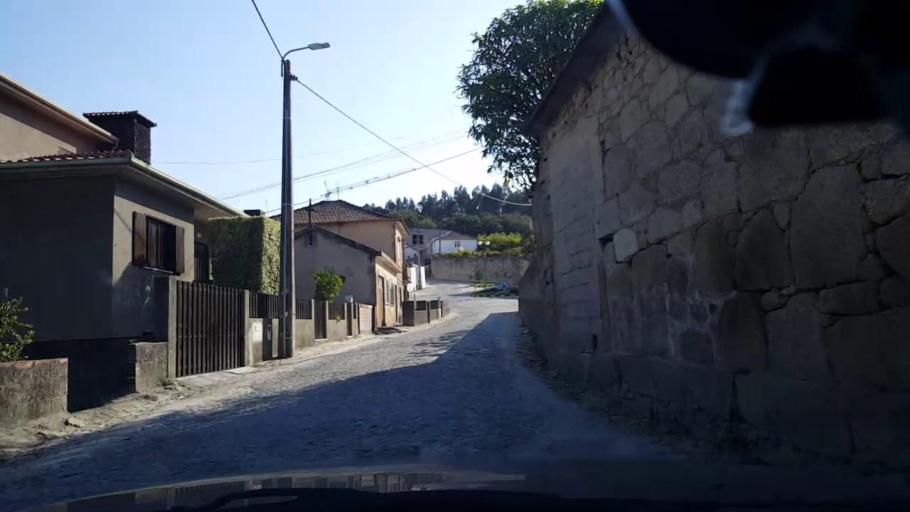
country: PT
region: Porto
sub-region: Vila do Conde
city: Arvore
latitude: 41.3573
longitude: -8.7220
